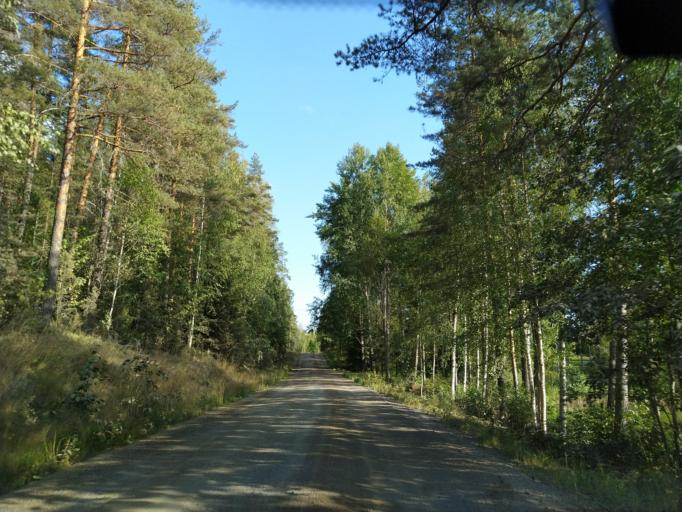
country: FI
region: Central Finland
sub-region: Jaemsae
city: Kuhmoinen
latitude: 61.7109
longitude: 24.9096
